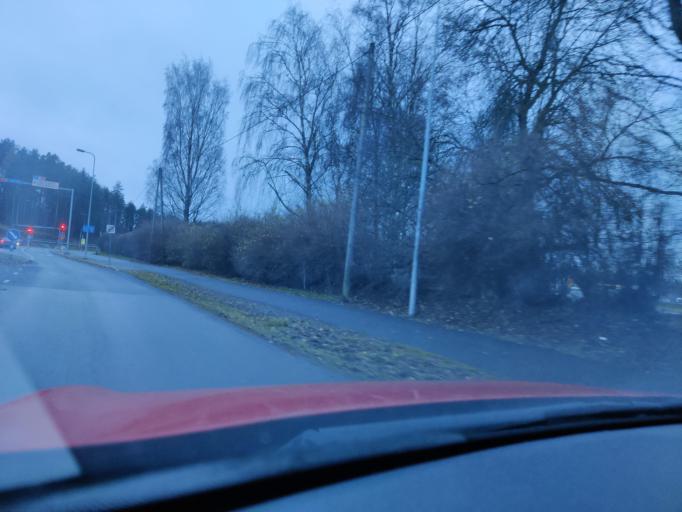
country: FI
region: Pirkanmaa
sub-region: Tampere
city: Nokia
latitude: 61.4812
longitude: 23.5293
